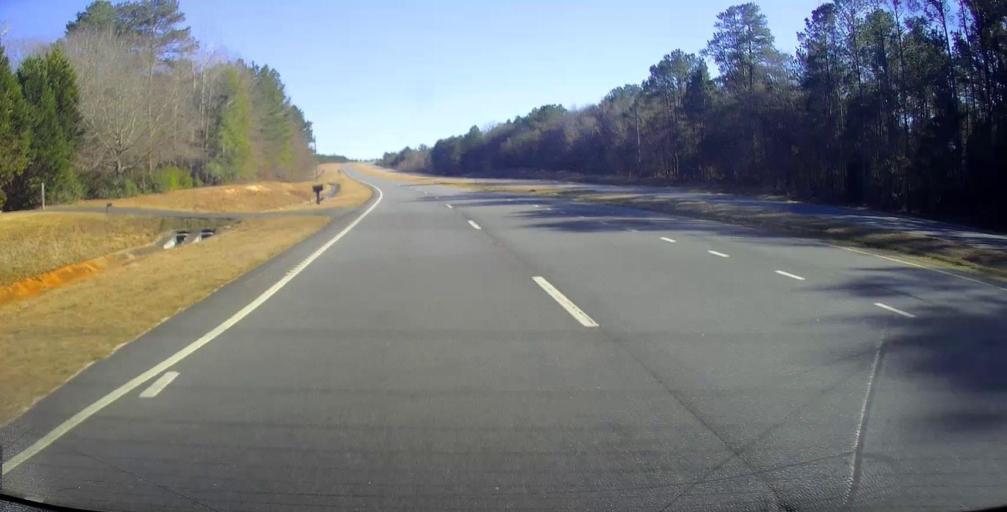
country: US
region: Georgia
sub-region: Taylor County
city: Butler
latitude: 32.6166
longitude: -84.2440
